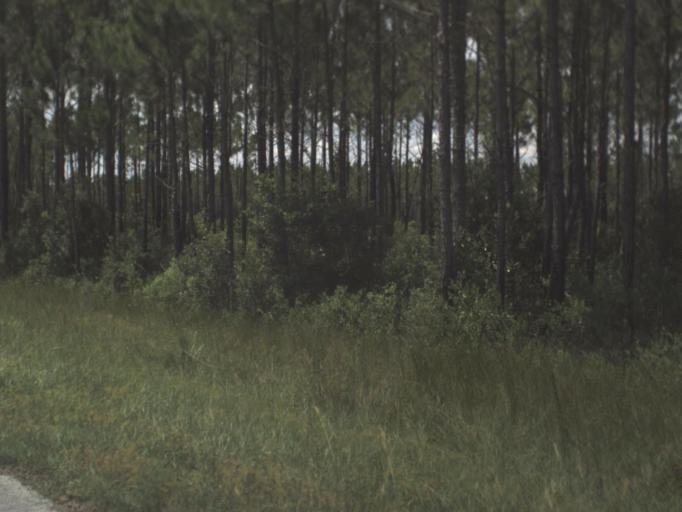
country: US
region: Florida
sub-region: Baker County
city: Macclenny
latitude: 30.5537
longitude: -82.3677
